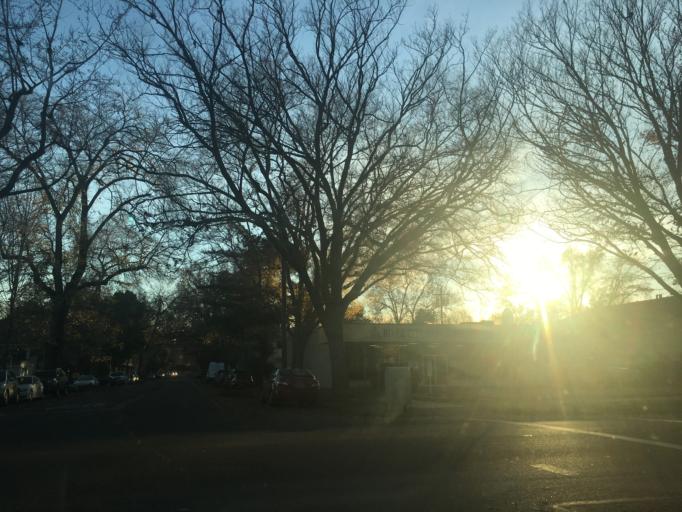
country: US
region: California
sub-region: Sacramento County
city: Sacramento
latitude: 38.5682
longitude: -121.4940
